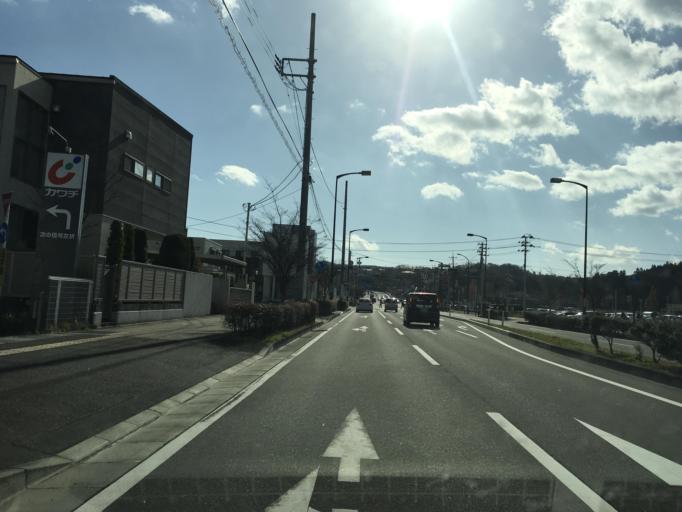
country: JP
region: Miyagi
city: Sendai
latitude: 38.2699
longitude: 140.7616
